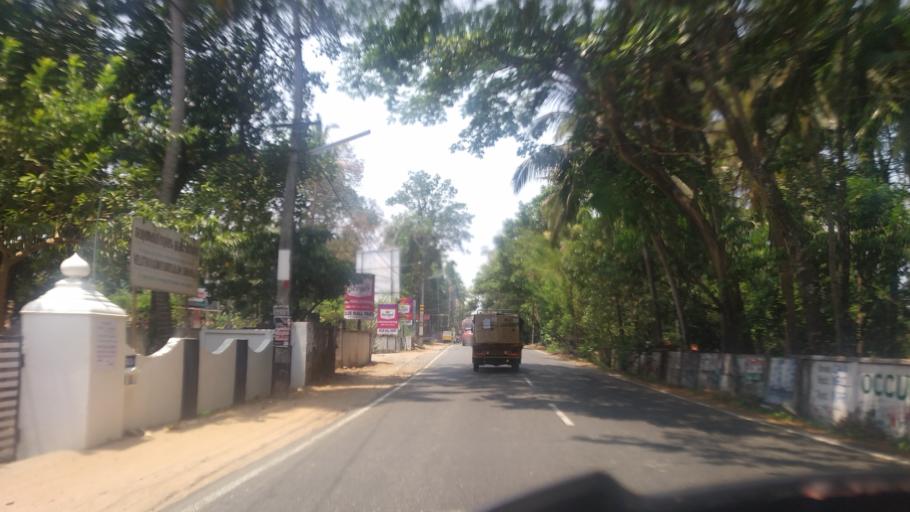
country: IN
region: Kerala
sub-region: Thrissur District
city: Kodungallur
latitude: 10.2685
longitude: 76.1787
